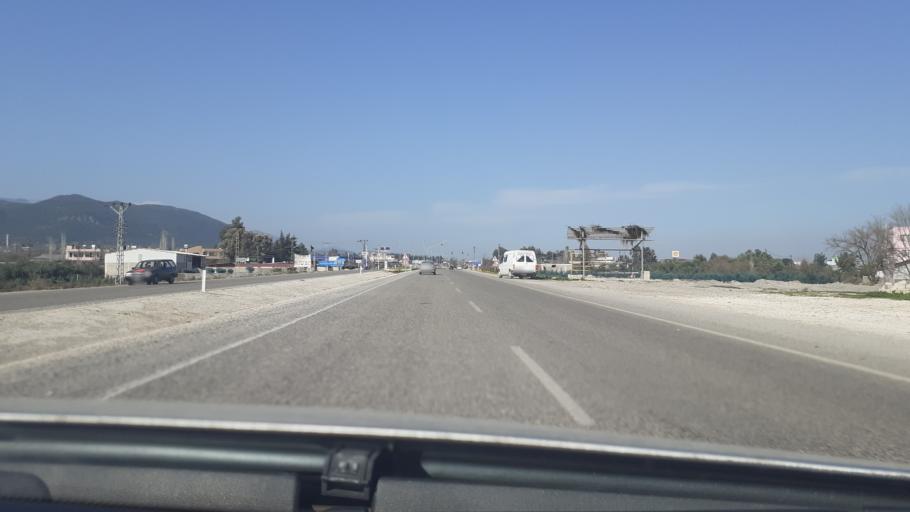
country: TR
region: Hatay
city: Aktepe
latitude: 36.6896
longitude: 36.4731
